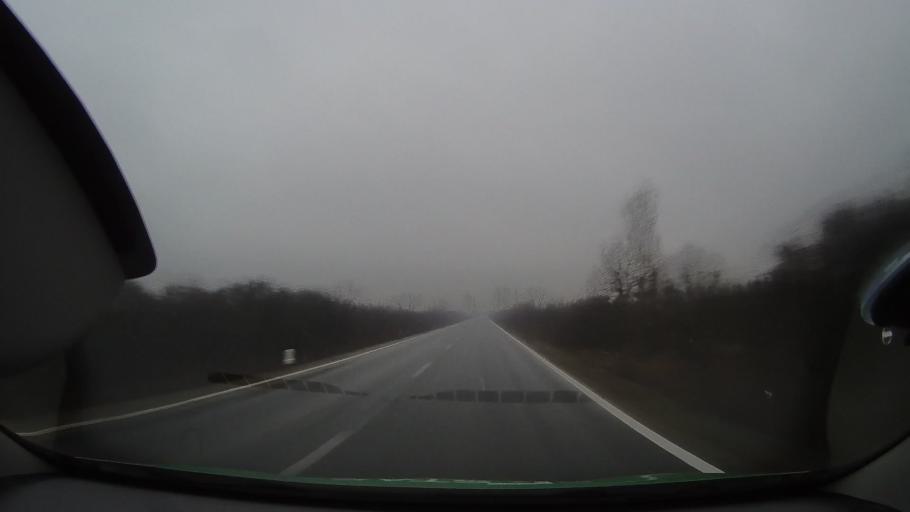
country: RO
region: Bihor
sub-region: Comuna Tinca
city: Tinca
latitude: 46.7523
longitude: 21.9371
